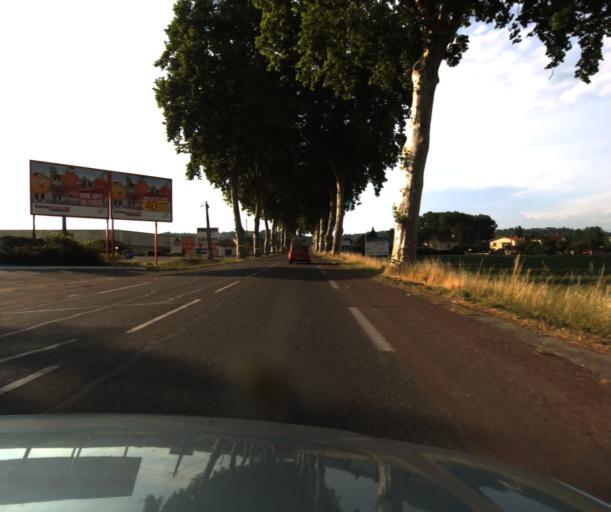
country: FR
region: Midi-Pyrenees
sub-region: Departement du Tarn-et-Garonne
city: Moissac
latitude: 44.0912
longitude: 1.0874
